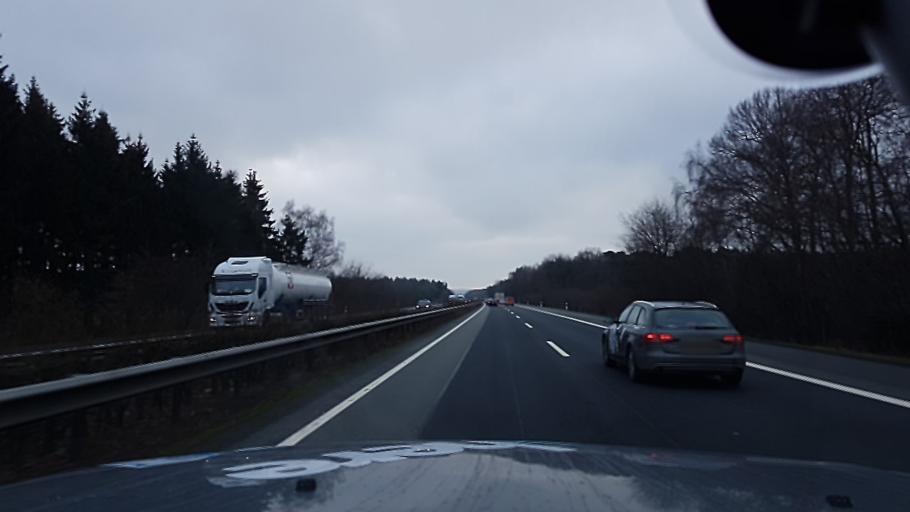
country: DE
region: Lower Saxony
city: Rieste
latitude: 52.4360
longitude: 8.0336
